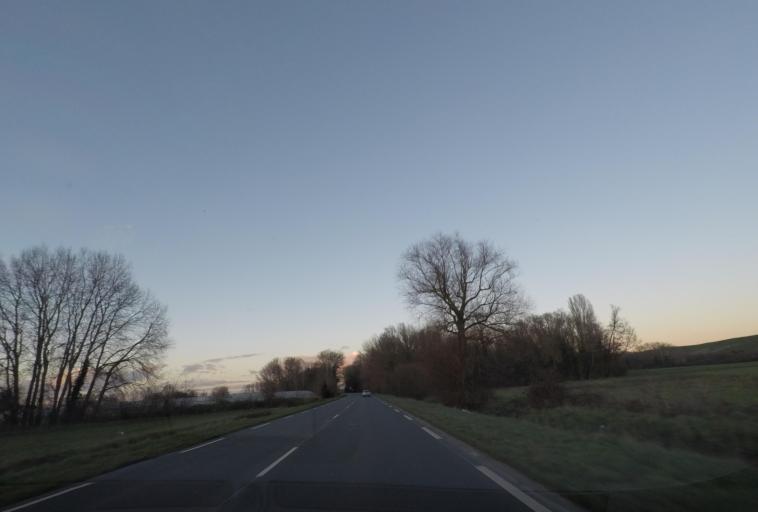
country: FR
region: Ile-de-France
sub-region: Departement de l'Essonne
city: Vert-le-Grand
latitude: 48.5802
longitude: 2.3668
